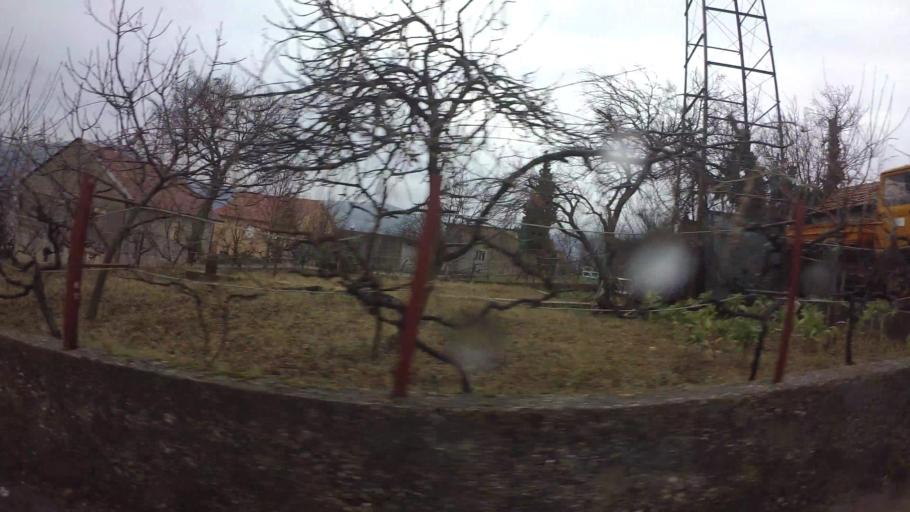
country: BA
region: Federation of Bosnia and Herzegovina
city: Cim
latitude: 43.3544
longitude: 17.7826
